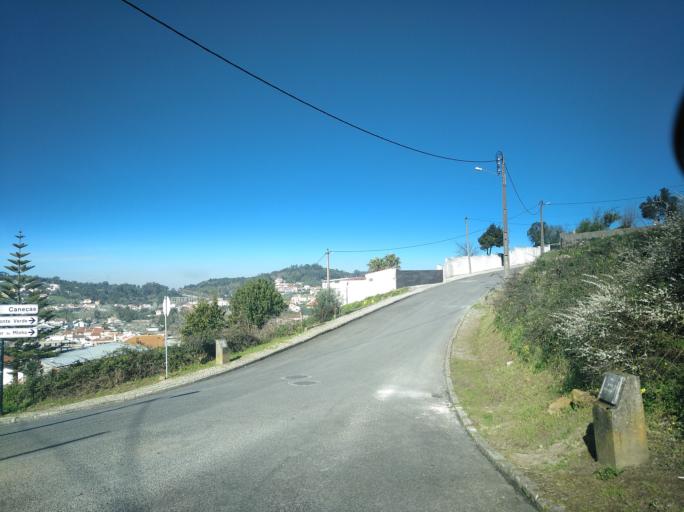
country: PT
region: Lisbon
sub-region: Odivelas
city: Canecas
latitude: 38.8094
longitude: -9.2212
